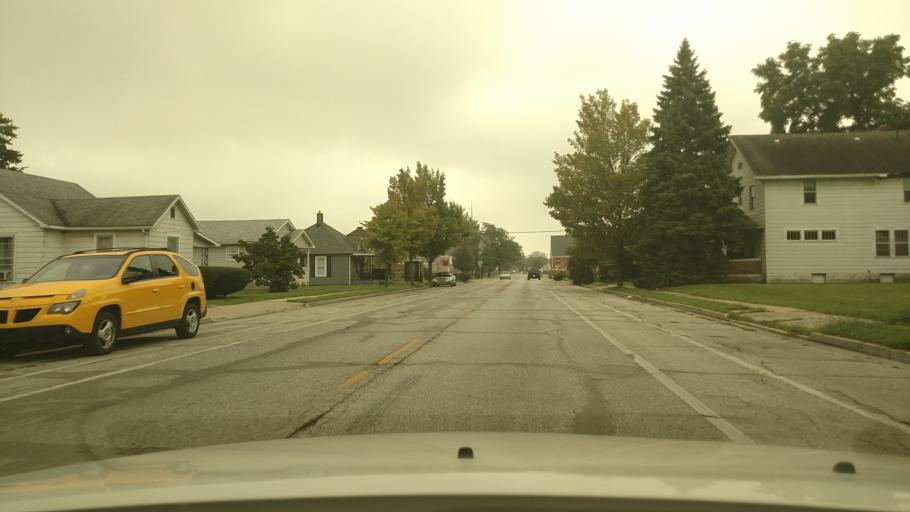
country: US
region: Indiana
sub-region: Howard County
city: Kokomo
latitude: 40.4953
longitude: -86.1270
